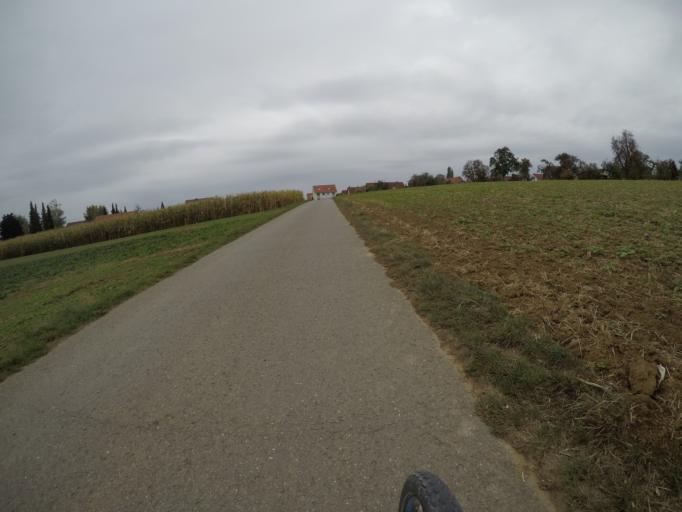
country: DE
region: Baden-Wuerttemberg
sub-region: Regierungsbezirk Stuttgart
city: Eberdingen
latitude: 48.8548
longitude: 8.9868
